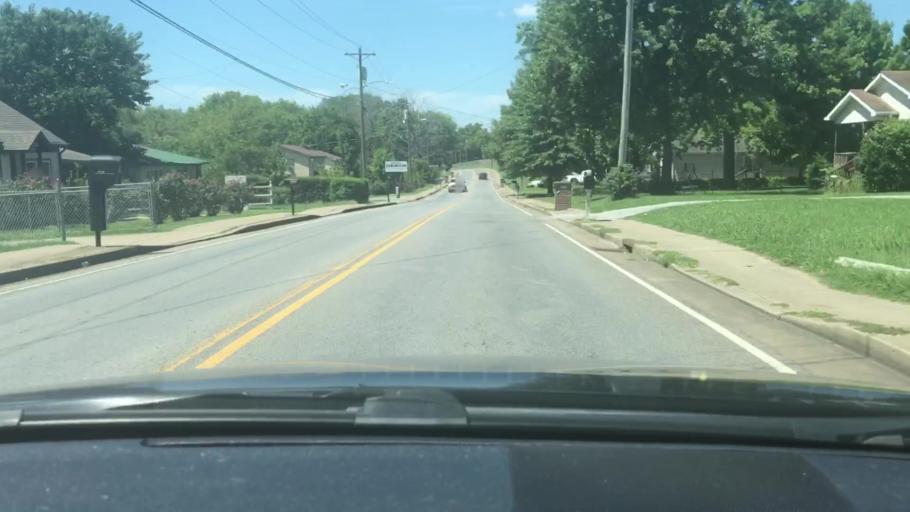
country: US
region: Tennessee
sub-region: Sumner County
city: Gallatin
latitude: 36.3931
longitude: -86.4601
